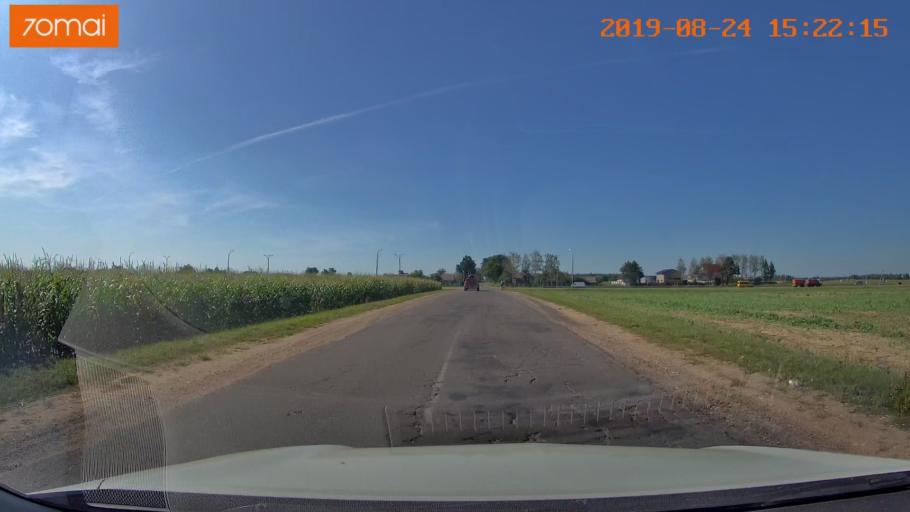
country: BY
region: Minsk
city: Samakhvalavichy
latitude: 53.6772
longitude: 27.5045
